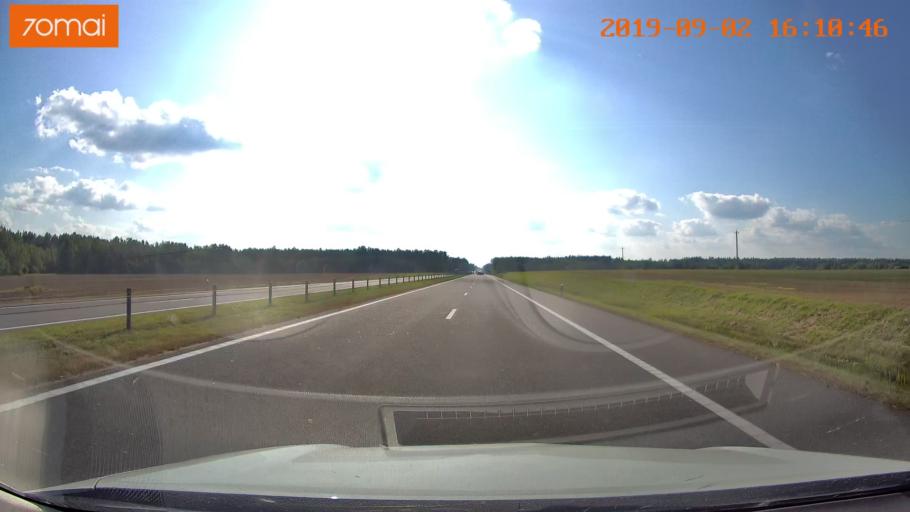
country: BY
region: Minsk
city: Chervyen'
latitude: 53.7616
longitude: 28.6623
